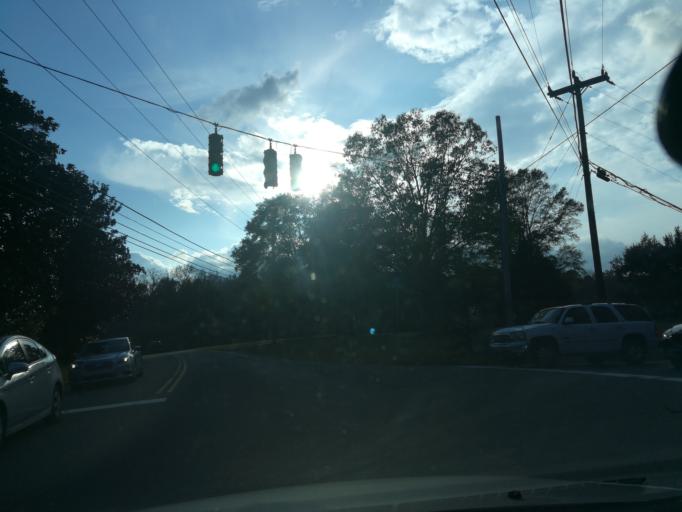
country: US
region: North Carolina
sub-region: Orange County
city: Chapel Hill
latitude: 35.9759
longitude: -79.0064
